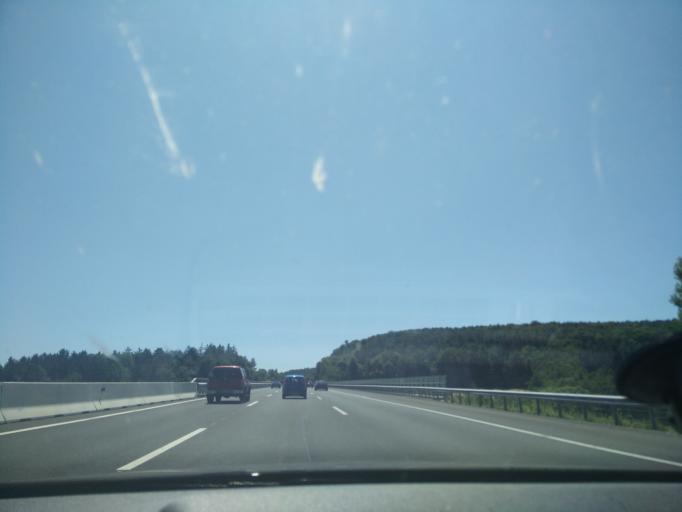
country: AT
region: Styria
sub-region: Politischer Bezirk Hartberg-Fuerstenfeld
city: Bad Waltersdorf
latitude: 47.1681
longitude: 15.9992
